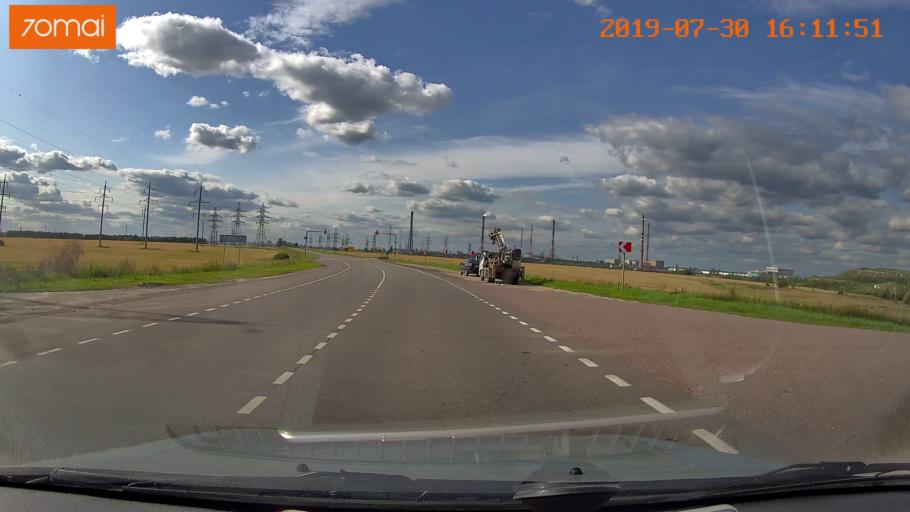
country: RU
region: Moskovskaya
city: Lopatinskiy
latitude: 55.2819
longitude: 38.7065
